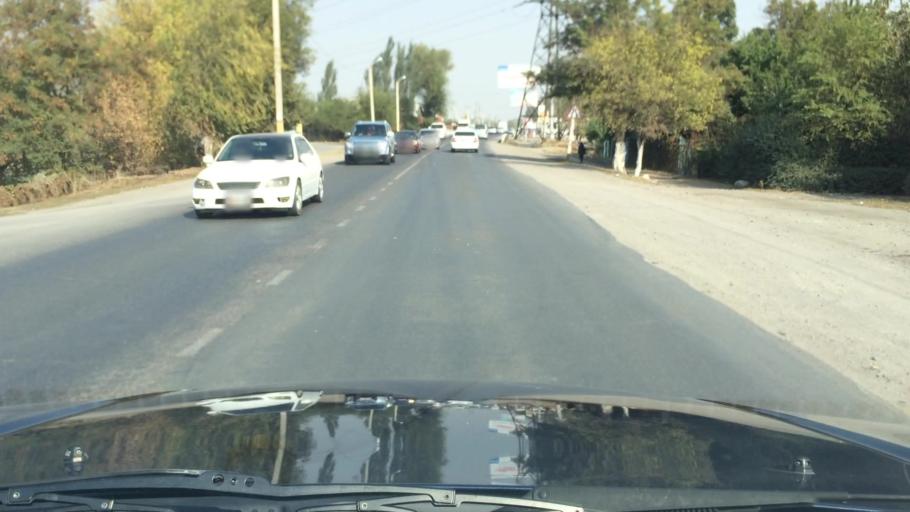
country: KG
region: Chuy
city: Lebedinovka
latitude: 42.8876
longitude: 74.6789
